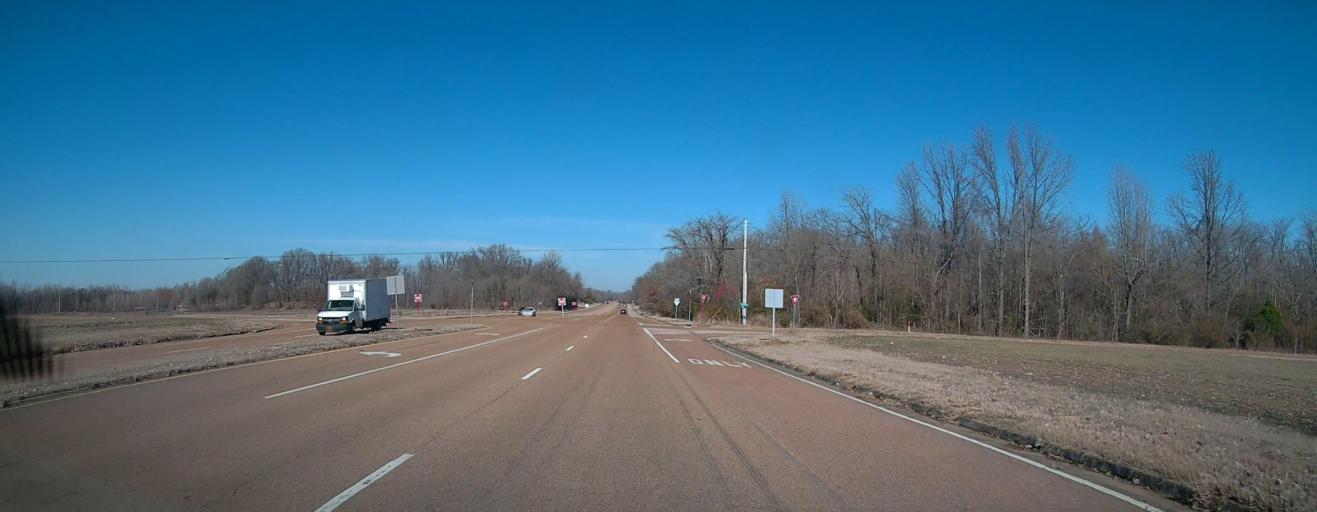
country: US
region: Tennessee
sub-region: Shelby County
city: Bartlett
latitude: 35.2603
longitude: -89.8895
